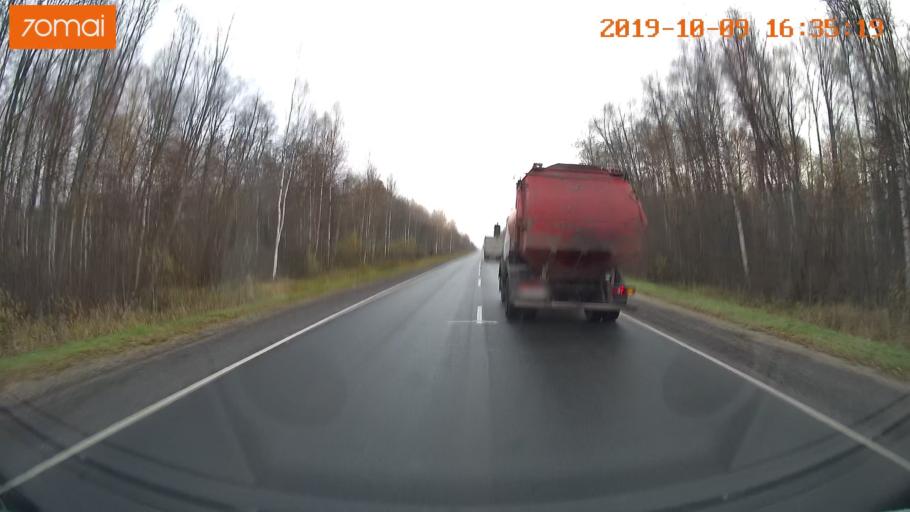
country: RU
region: Kostroma
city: Oktyabr'skiy
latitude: 57.5571
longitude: 40.9997
